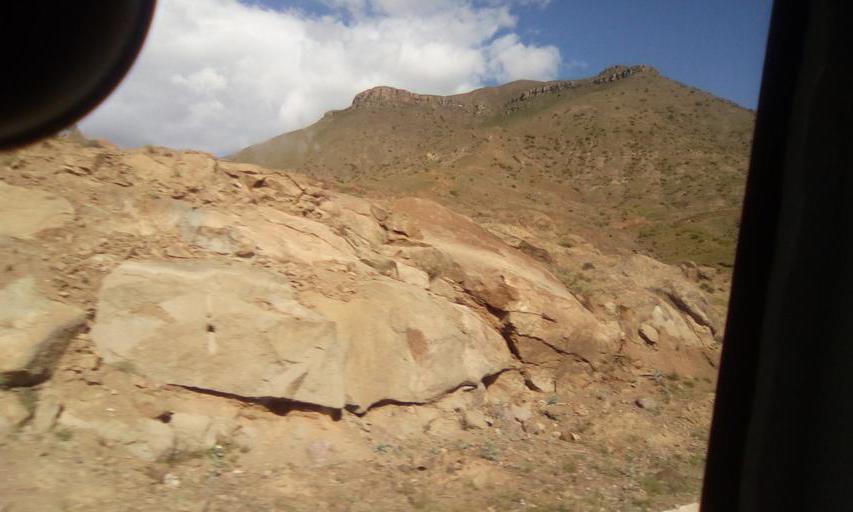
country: LS
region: Qacha's Nek
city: Qacha's Nek
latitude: -30.0179
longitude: 28.1760
